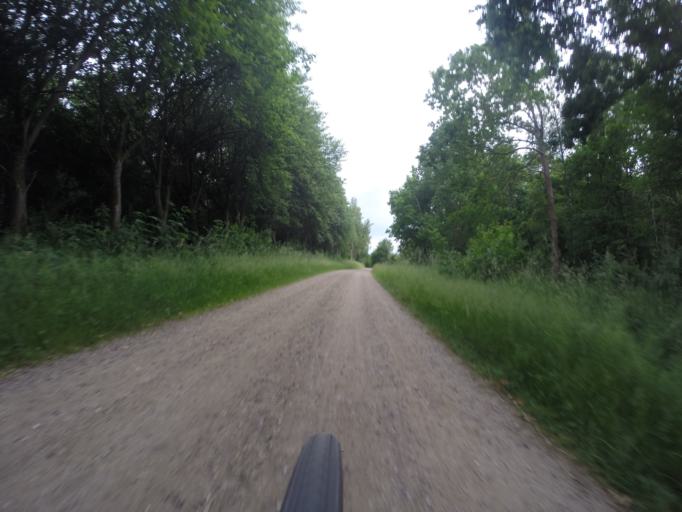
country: DK
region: Capital Region
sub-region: Albertslund Kommune
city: Albertslund
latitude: 55.6916
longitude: 12.3275
